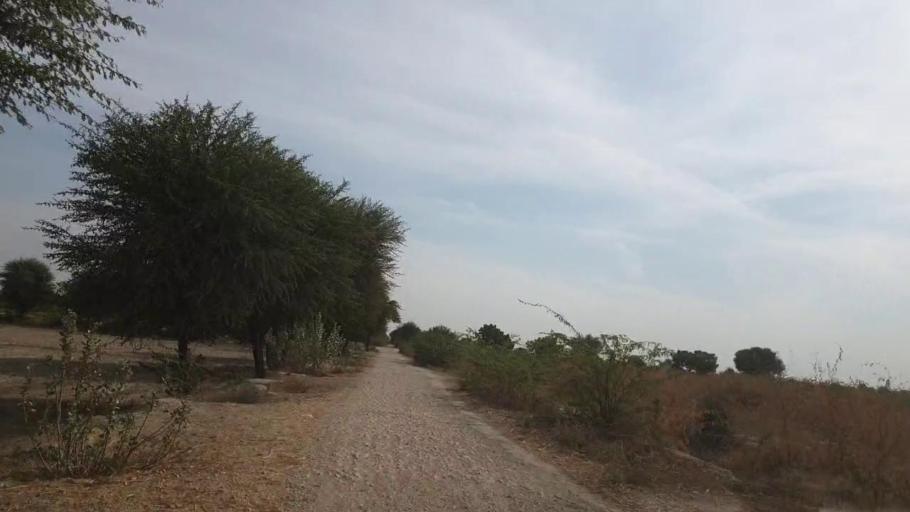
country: PK
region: Sindh
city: Nabisar
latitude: 25.0245
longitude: 69.5623
